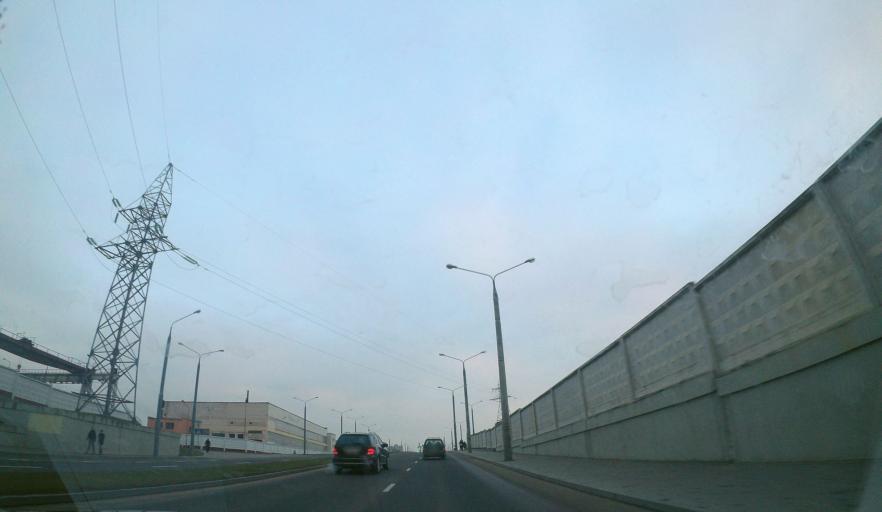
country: BY
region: Grodnenskaya
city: Hrodna
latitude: 53.6542
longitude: 23.7894
